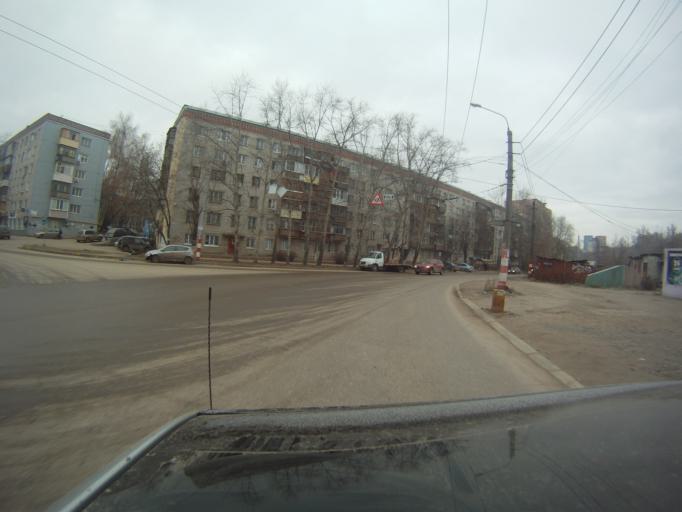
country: RU
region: Nizjnij Novgorod
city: Afonino
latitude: 56.2902
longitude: 44.0526
